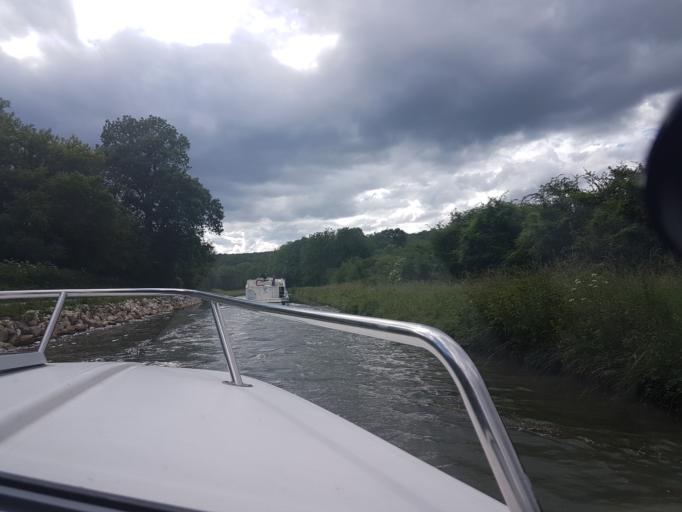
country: FR
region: Bourgogne
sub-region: Departement de l'Yonne
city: Vermenton
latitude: 47.5574
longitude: 3.6398
